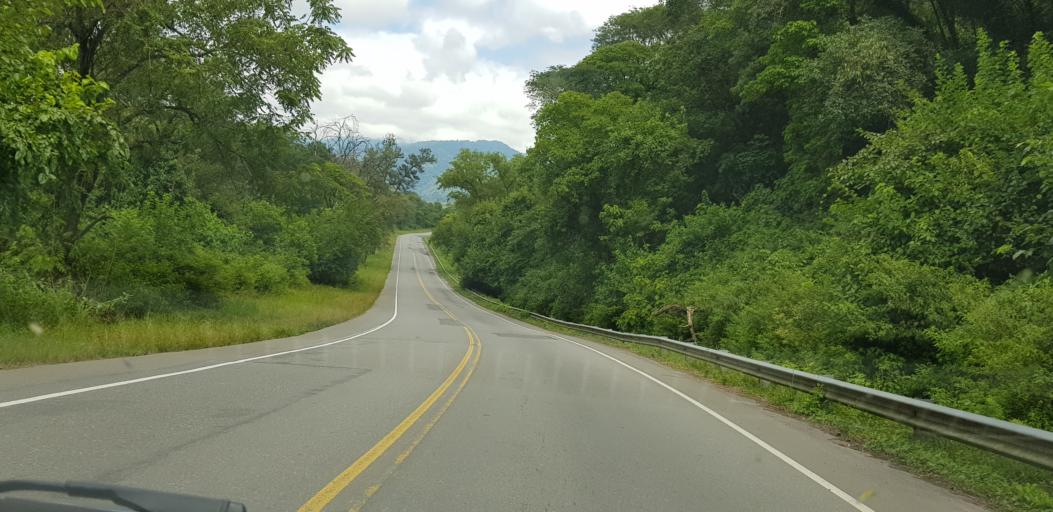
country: AR
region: Tucuman
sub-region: Departamento de Monteros
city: Monteros
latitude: -27.0997
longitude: -65.5906
